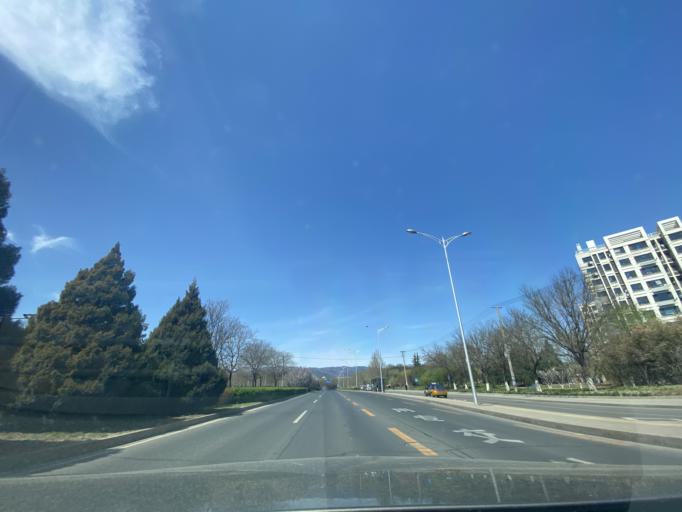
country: CN
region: Beijing
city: Sijiqing
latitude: 39.9356
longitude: 116.2437
